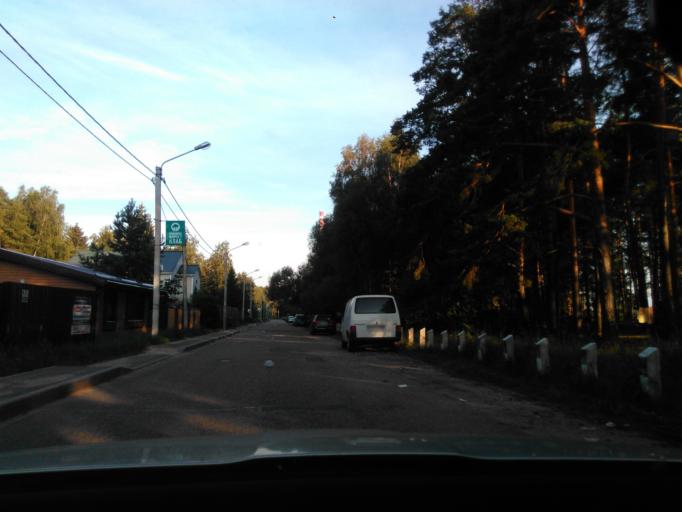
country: RU
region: Tverskaya
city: Konakovo
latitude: 56.7517
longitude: 36.7570
